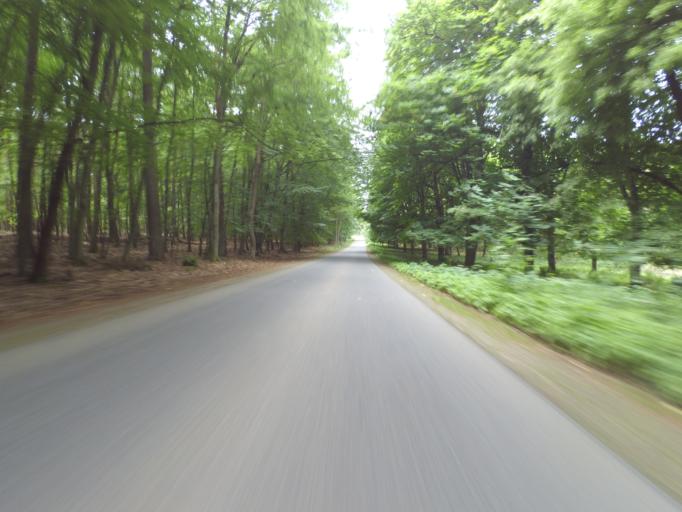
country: DE
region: Mecklenburg-Vorpommern
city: Krakow am See
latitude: 53.5954
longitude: 12.3813
